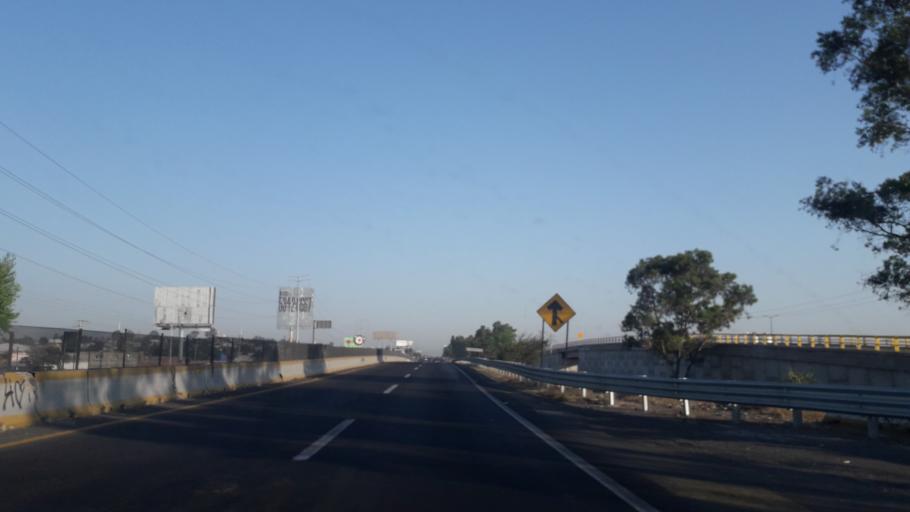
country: MX
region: Puebla
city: Ocotlan
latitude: 19.1376
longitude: -98.2741
